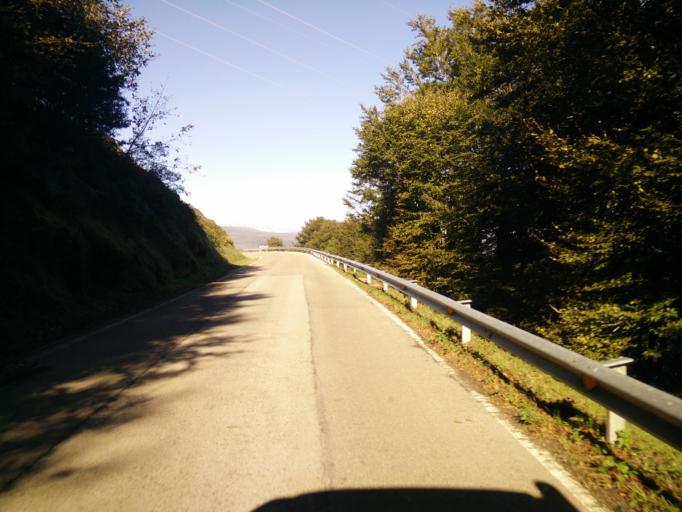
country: ES
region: Cantabria
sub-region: Provincia de Cantabria
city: San Pedro del Romeral
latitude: 43.0523
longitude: -3.8471
